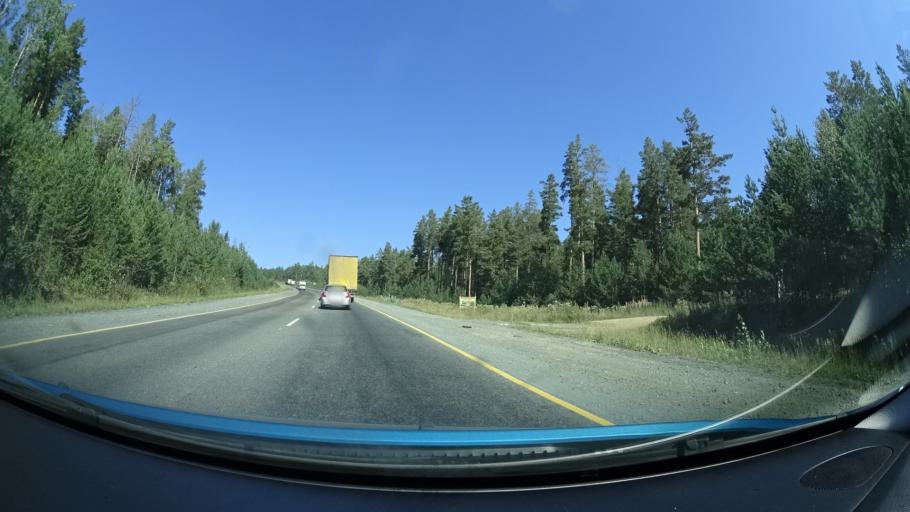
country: RU
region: Bashkortostan
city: Abzakovo
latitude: 53.8859
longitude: 58.5279
